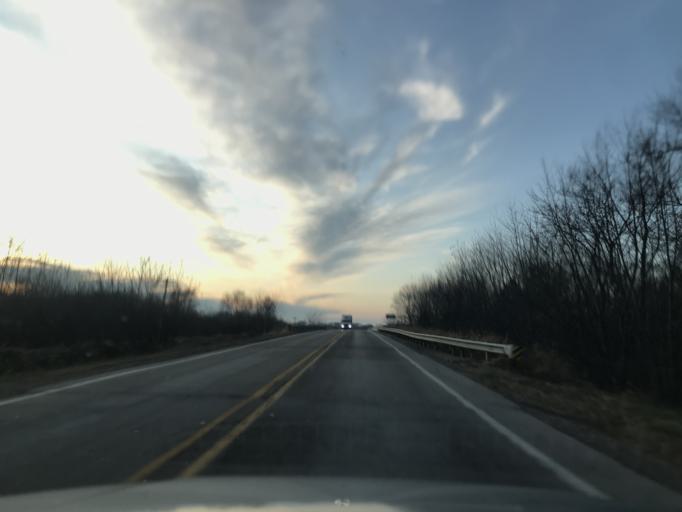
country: US
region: Illinois
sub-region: Henderson County
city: Oquawka
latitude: 41.0190
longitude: -90.8080
